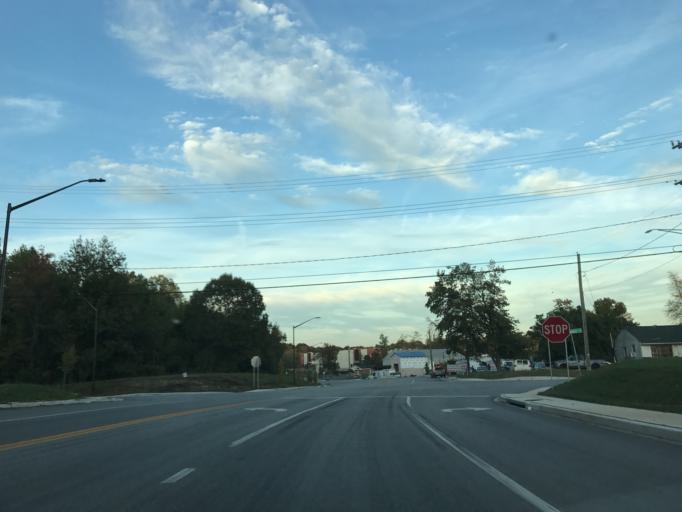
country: US
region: Maryland
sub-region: Anne Arundel County
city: Jessup
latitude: 39.1641
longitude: -76.7708
